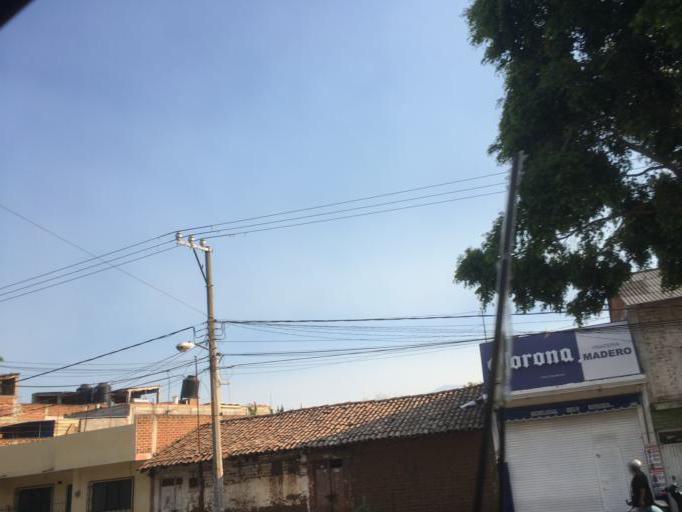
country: MX
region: Michoacan
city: Quiroga
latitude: 19.6650
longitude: -101.5293
